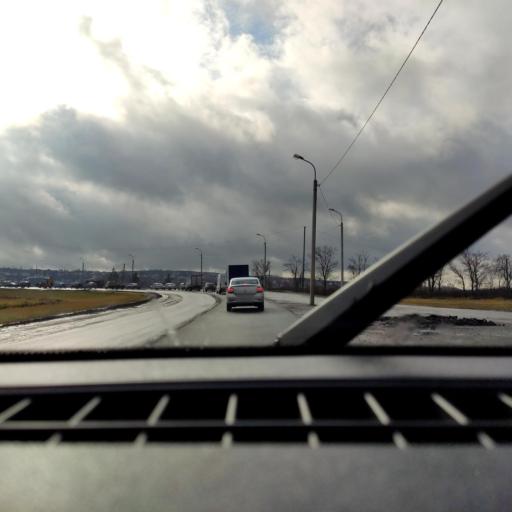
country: RU
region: Bashkortostan
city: Kabakovo
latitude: 54.6452
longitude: 56.0822
